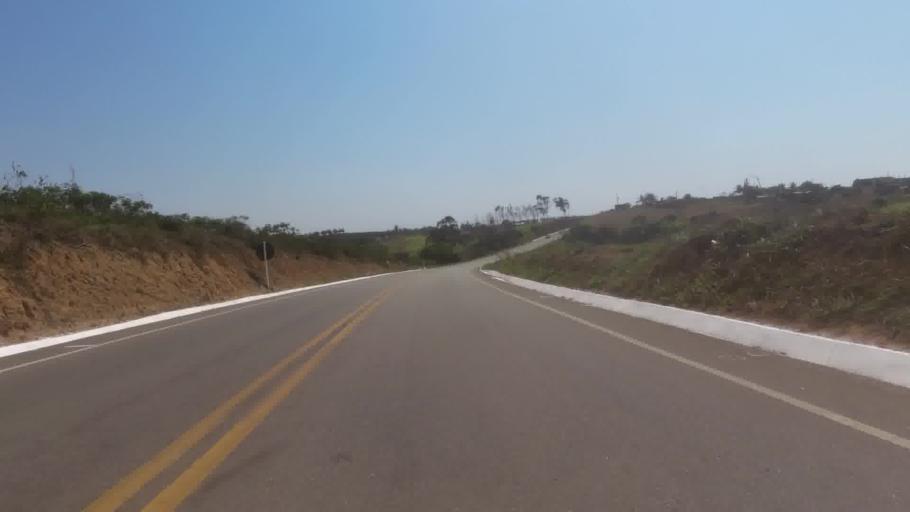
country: BR
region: Espirito Santo
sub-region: Marataizes
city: Marataizes
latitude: -21.0877
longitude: -40.8500
